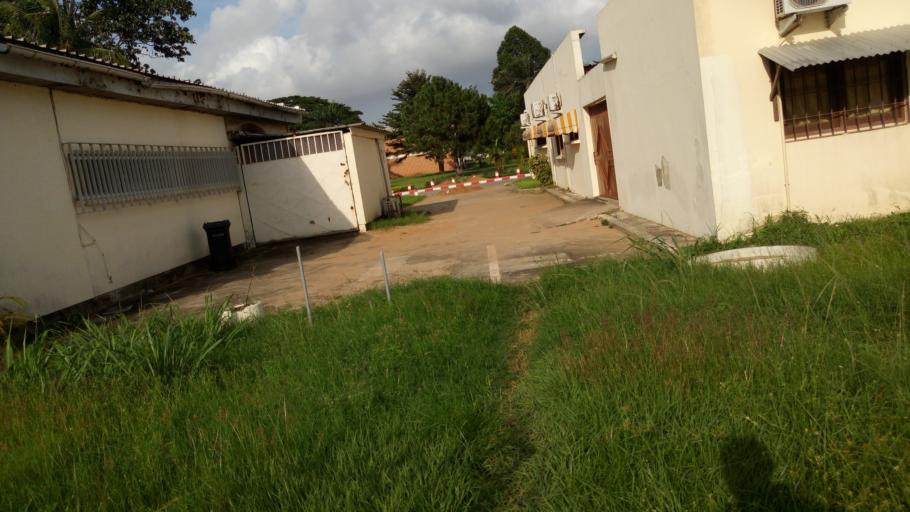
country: CI
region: Lagunes
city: Abidjan
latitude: 5.3428
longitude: -3.9882
